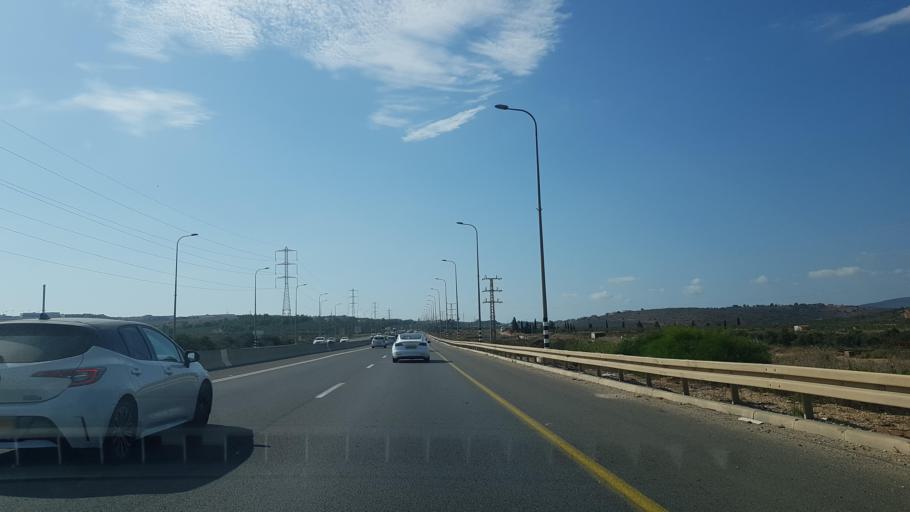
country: IL
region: Northern District
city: Kafr Kanna
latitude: 32.7630
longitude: 35.3363
